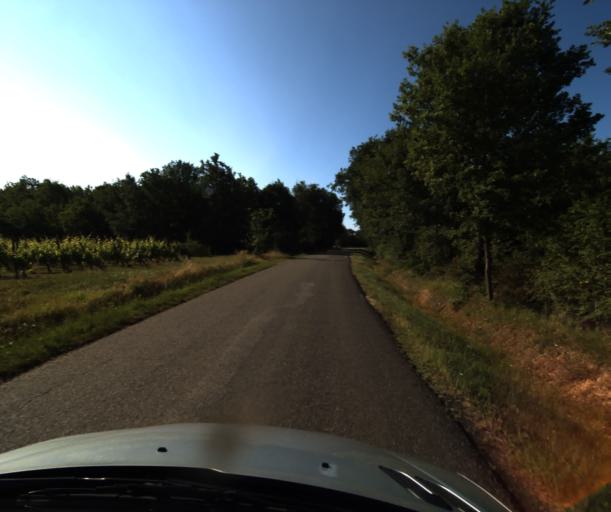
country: FR
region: Midi-Pyrenees
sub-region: Departement du Tarn-et-Garonne
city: Saint-Porquier
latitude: 44.0666
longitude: 1.2041
